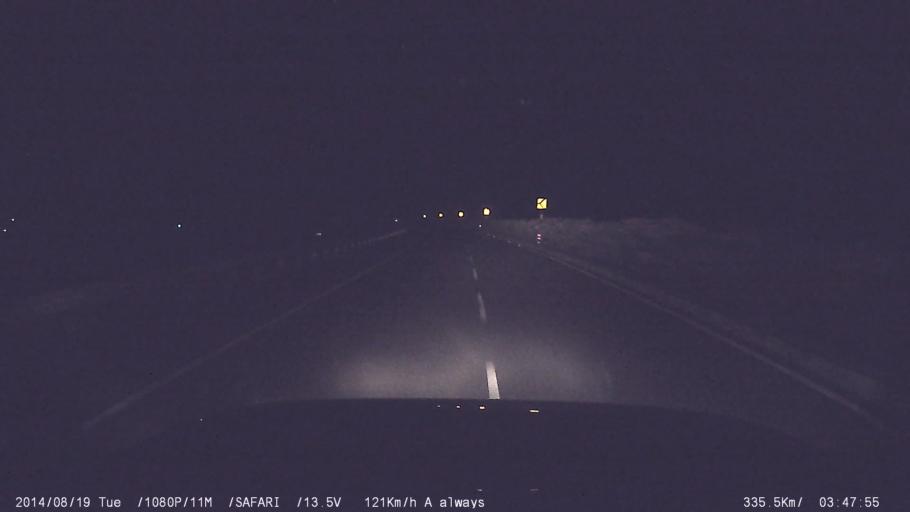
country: IN
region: Tamil Nadu
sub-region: Erode
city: Vijayapuri
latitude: 11.2386
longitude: 77.4995
